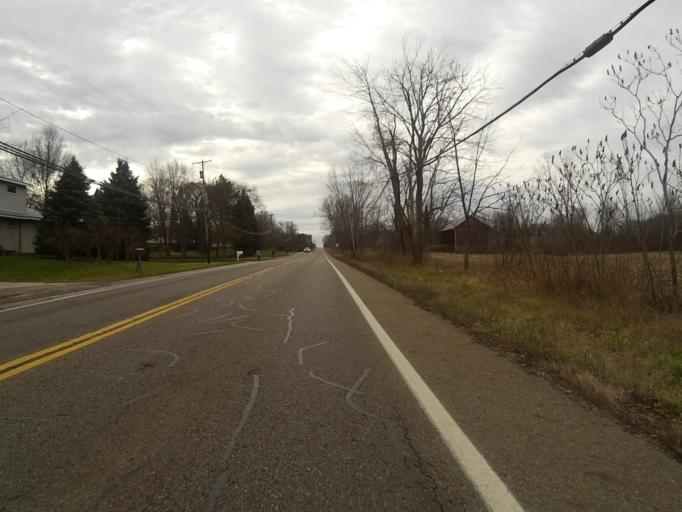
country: US
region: Ohio
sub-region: Portage County
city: Brimfield
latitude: 41.0959
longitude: -81.3464
